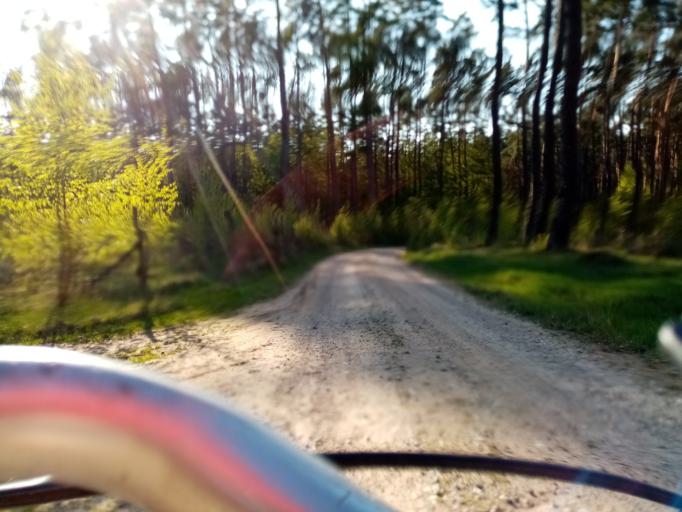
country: PL
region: Kujawsko-Pomorskie
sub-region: Powiat brodnicki
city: Gorzno
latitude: 53.1599
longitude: 19.6854
